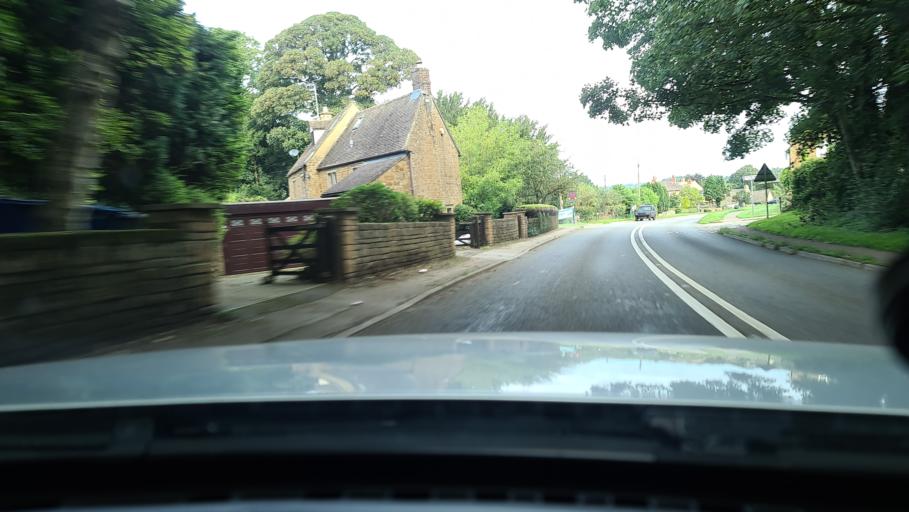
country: GB
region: England
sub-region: Oxfordshire
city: Hanwell
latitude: 52.0719
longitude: -1.3746
